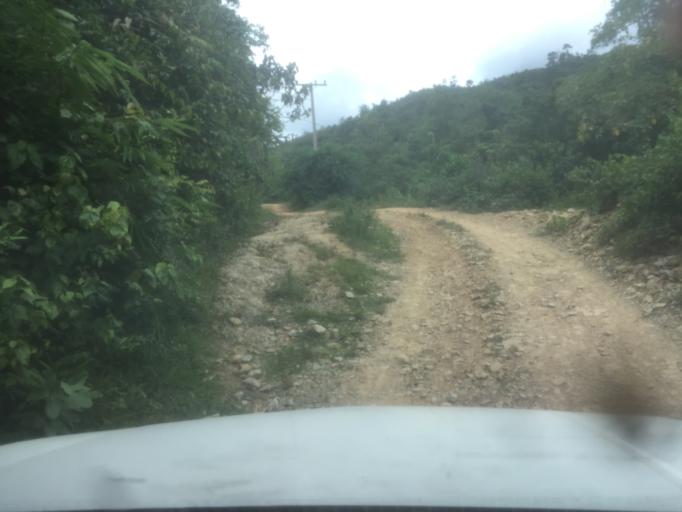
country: LA
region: Phongsali
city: Khoa
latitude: 20.9092
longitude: 102.5494
